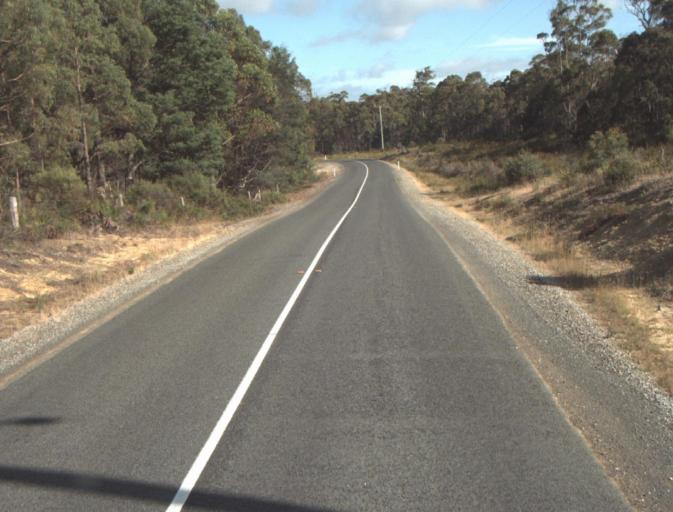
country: AU
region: Tasmania
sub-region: Dorset
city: Bridport
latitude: -41.1386
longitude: 147.2271
